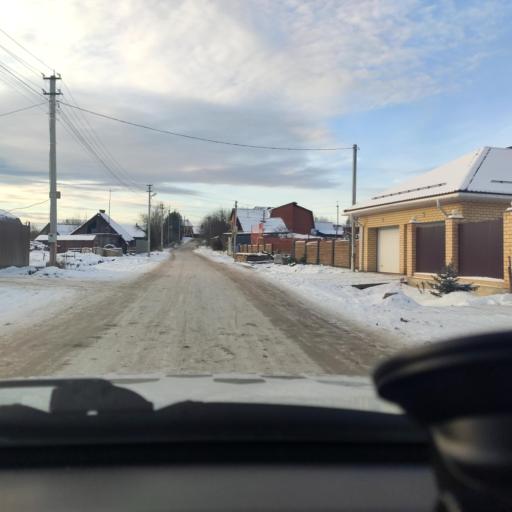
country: RU
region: Perm
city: Ferma
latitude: 57.9444
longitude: 56.3568
